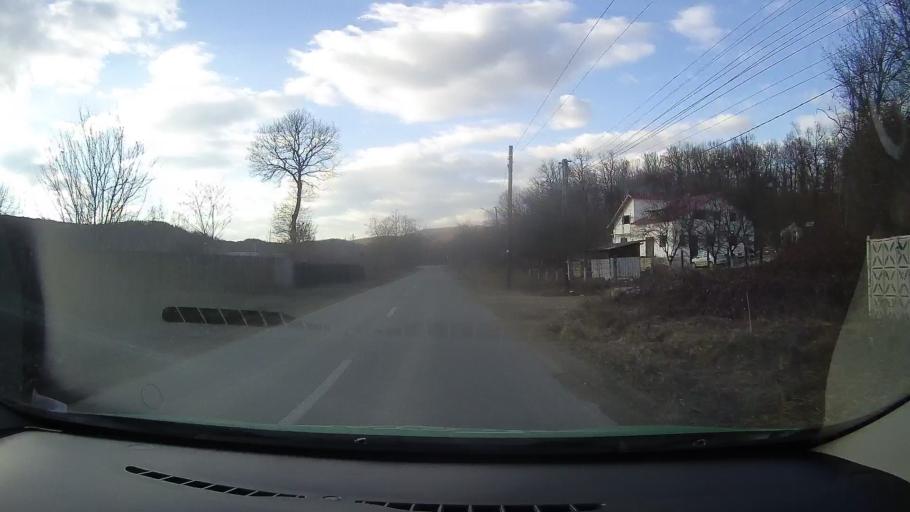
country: RO
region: Dambovita
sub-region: Comuna Ocnita
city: Ocnita
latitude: 44.9634
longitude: 25.5492
